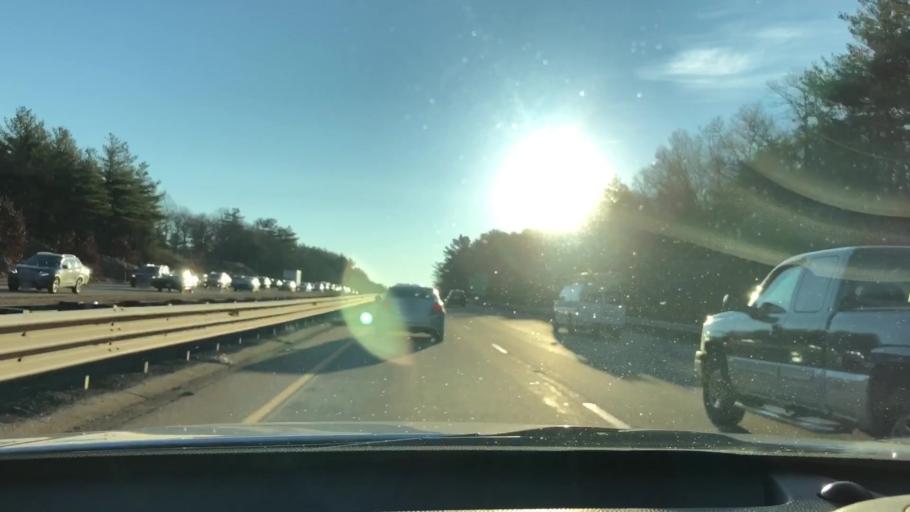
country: US
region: Massachusetts
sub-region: Norfolk County
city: Weymouth
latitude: 42.1846
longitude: -70.9260
